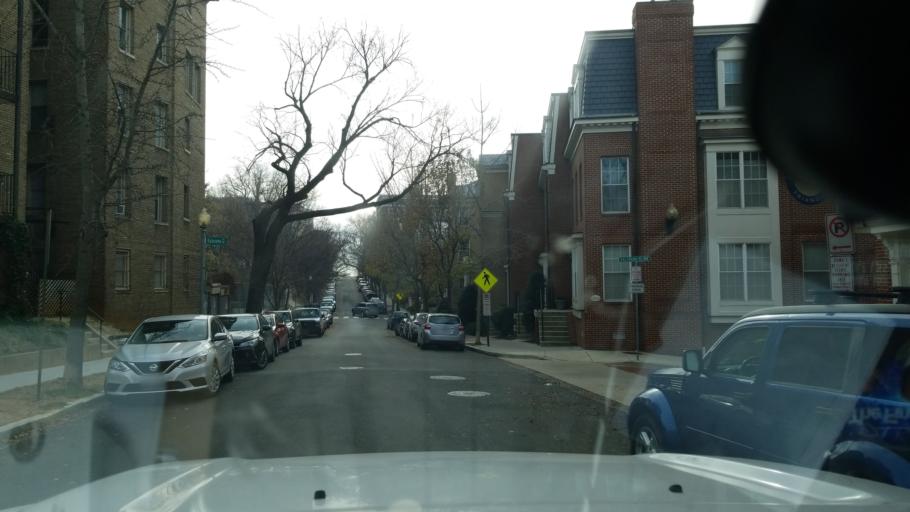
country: US
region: Washington, D.C.
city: Washington, D.C.
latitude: 38.9214
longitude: -77.0459
